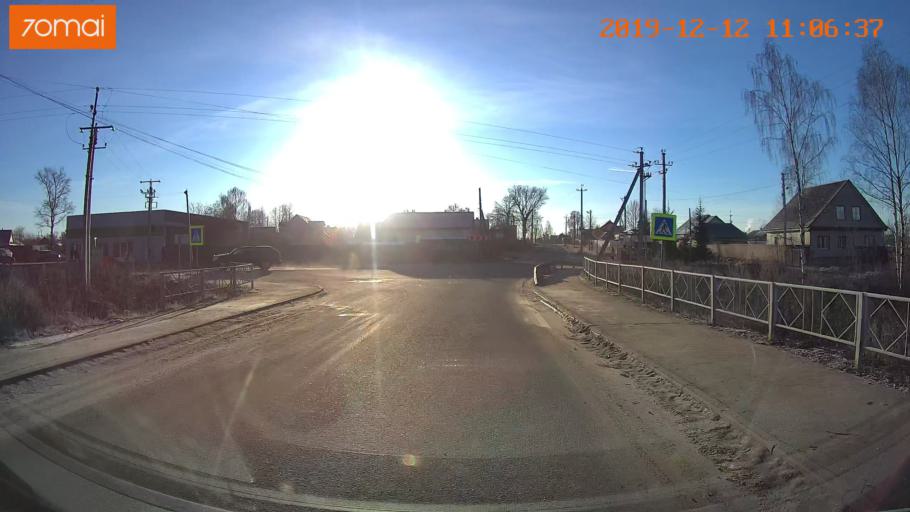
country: RU
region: Ivanovo
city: Kokhma
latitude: 56.9426
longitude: 41.0885
